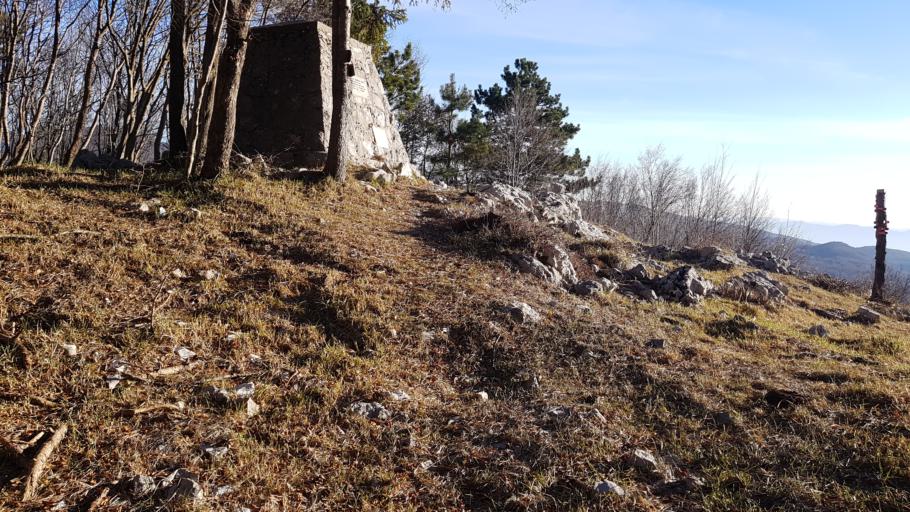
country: SI
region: Nova Gorica
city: Kromberk
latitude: 46.0151
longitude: 13.7088
